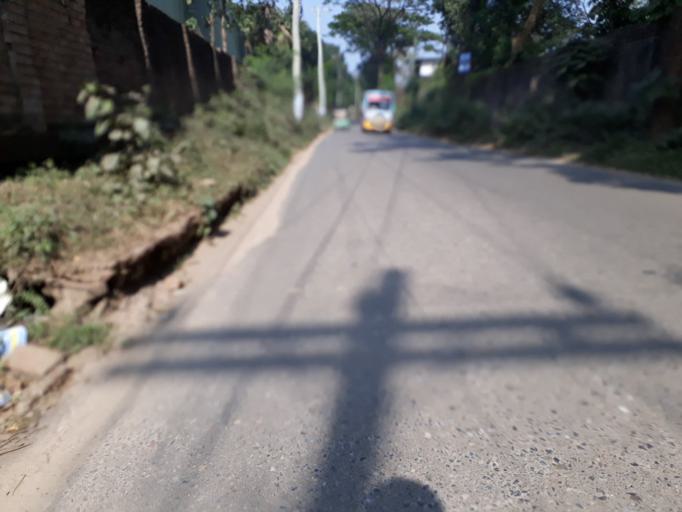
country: BD
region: Dhaka
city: Tungi
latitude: 23.8702
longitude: 90.3098
